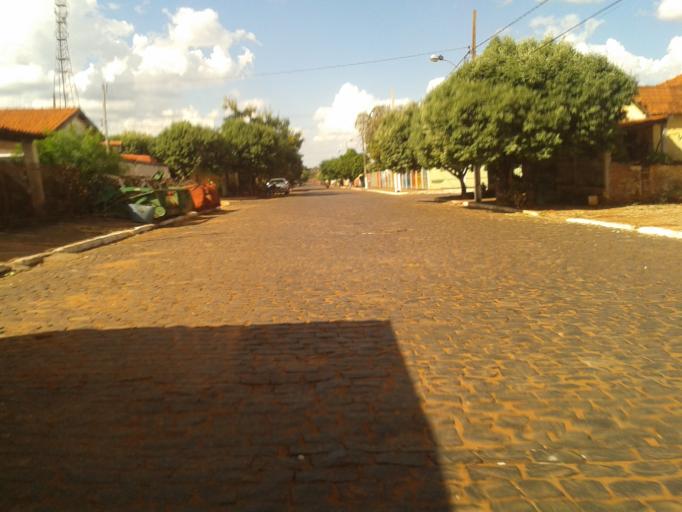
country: BR
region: Minas Gerais
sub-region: Santa Vitoria
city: Santa Vitoria
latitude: -18.6943
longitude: -49.9447
